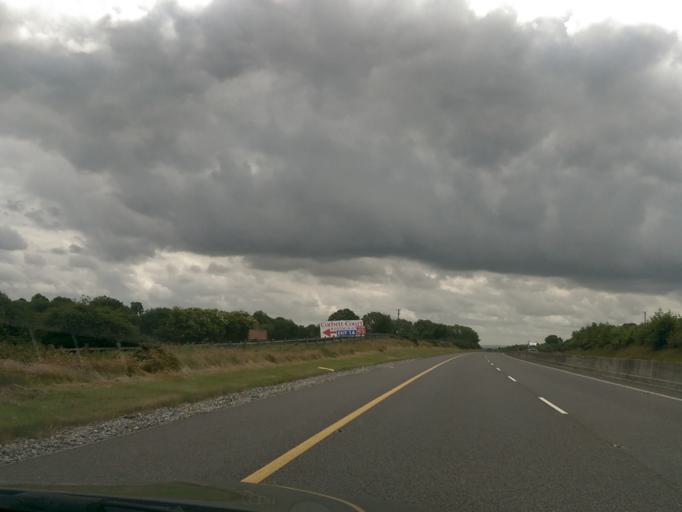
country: IE
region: Munster
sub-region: County Cork
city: Mitchelstown
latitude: 52.2051
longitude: -8.2742
